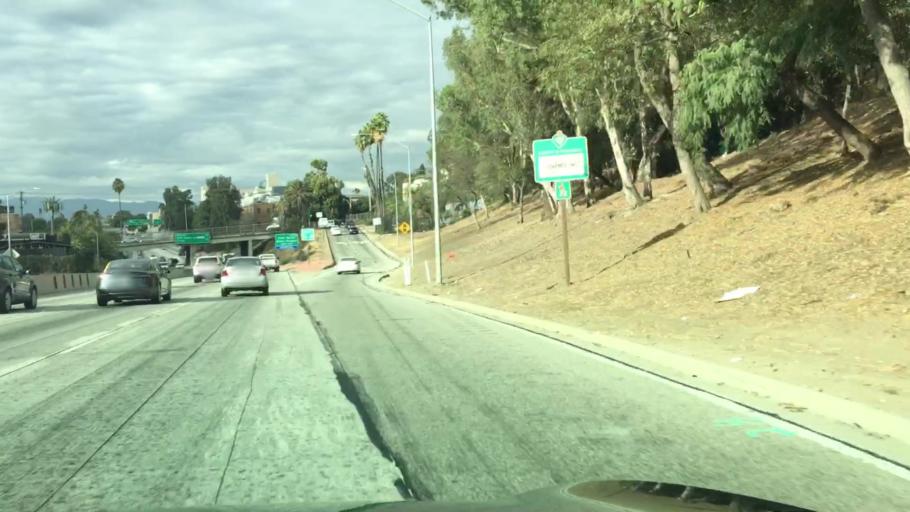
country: US
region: California
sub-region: Los Angeles County
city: Boyle Heights
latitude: 34.0408
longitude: -118.2213
